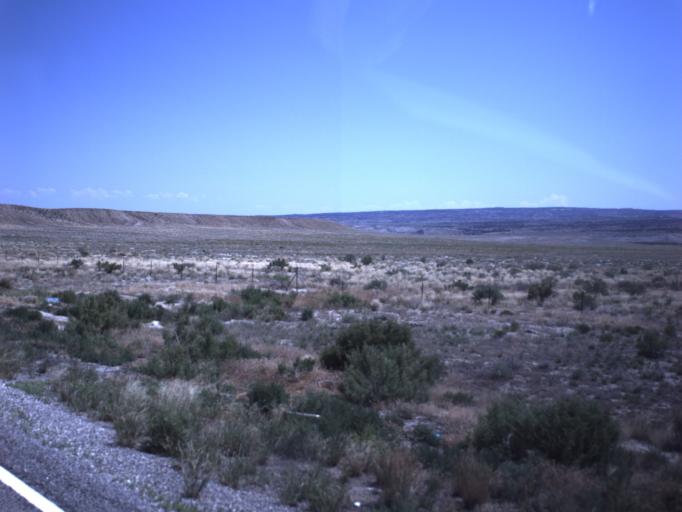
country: US
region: Utah
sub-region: Emery County
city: Ferron
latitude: 38.8472
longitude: -111.3104
